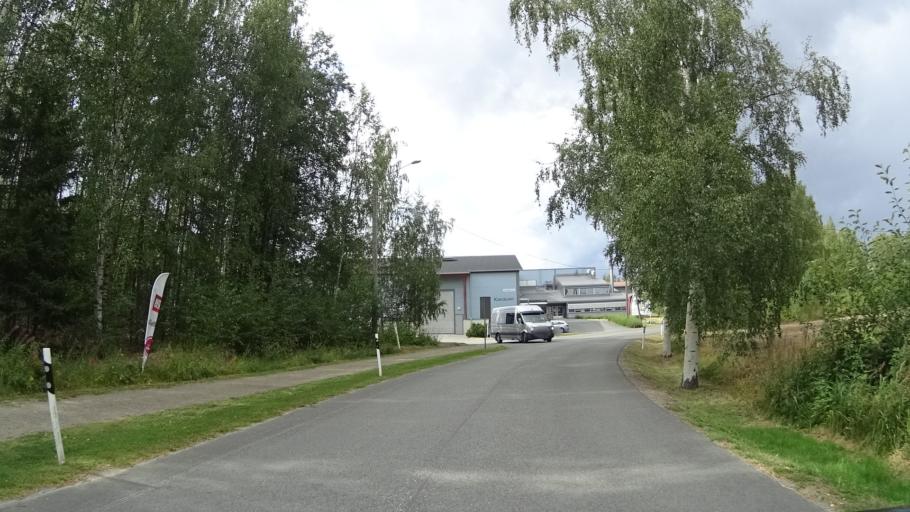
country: FI
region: Pirkanmaa
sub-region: Tampere
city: Kangasala
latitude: 61.4429
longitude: 24.1293
